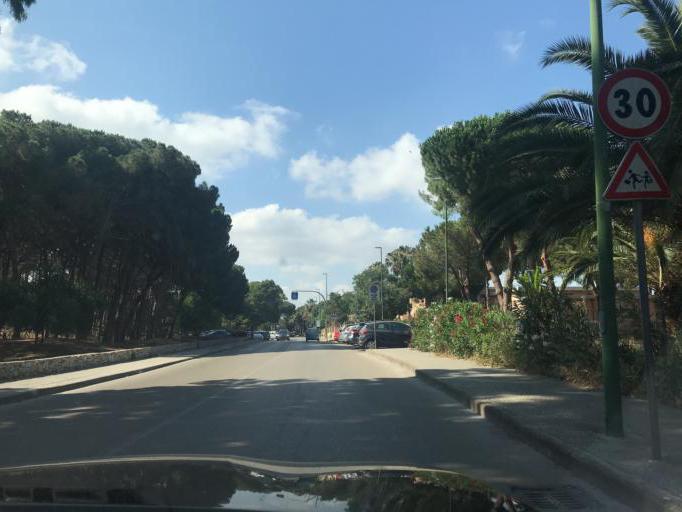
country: IT
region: Sardinia
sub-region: Provincia di Sassari
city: Alghero
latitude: 40.5817
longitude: 8.3117
